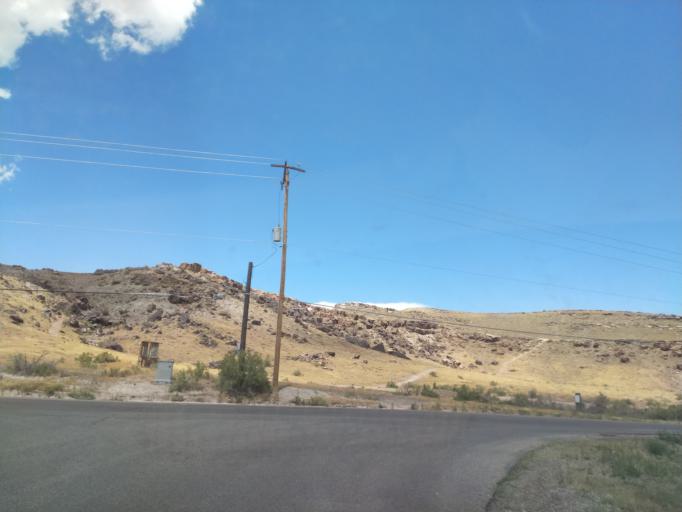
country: US
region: Colorado
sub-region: Mesa County
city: Redlands
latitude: 39.0725
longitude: -108.6492
